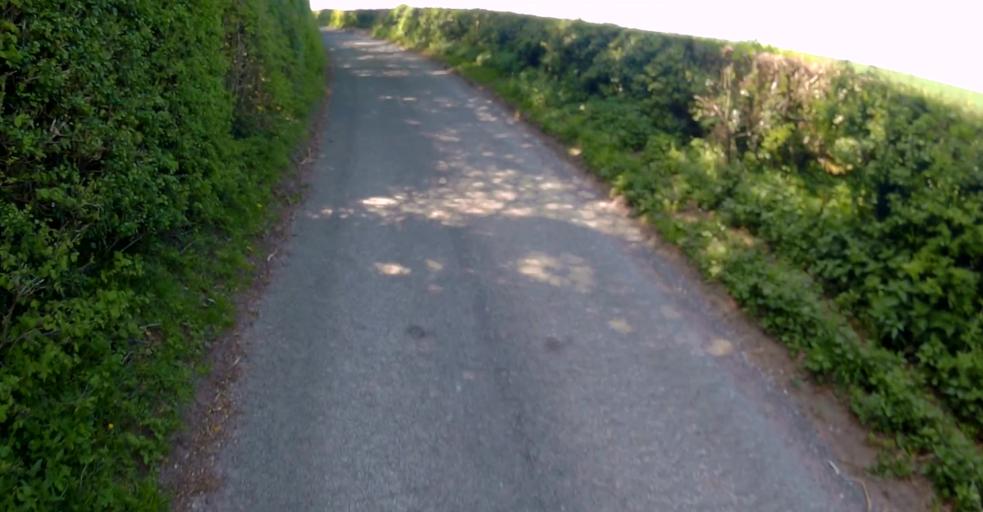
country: GB
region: England
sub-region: Hampshire
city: Overton
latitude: 51.2040
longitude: -1.2392
